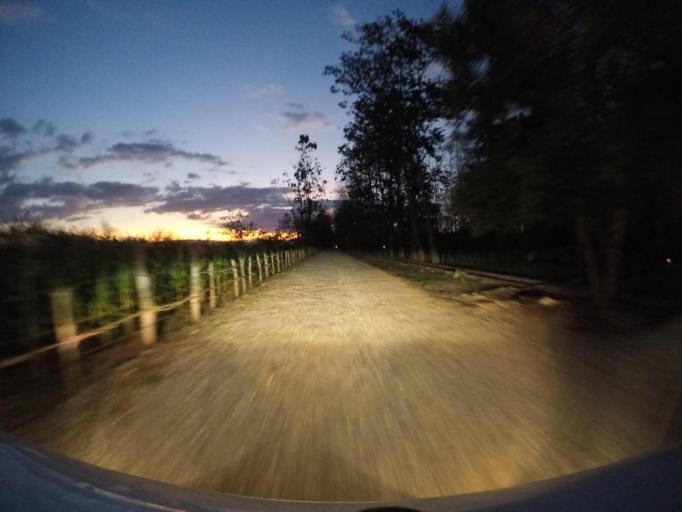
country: TL
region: Bobonaro
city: Maliana
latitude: -8.9715
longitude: 125.2150
